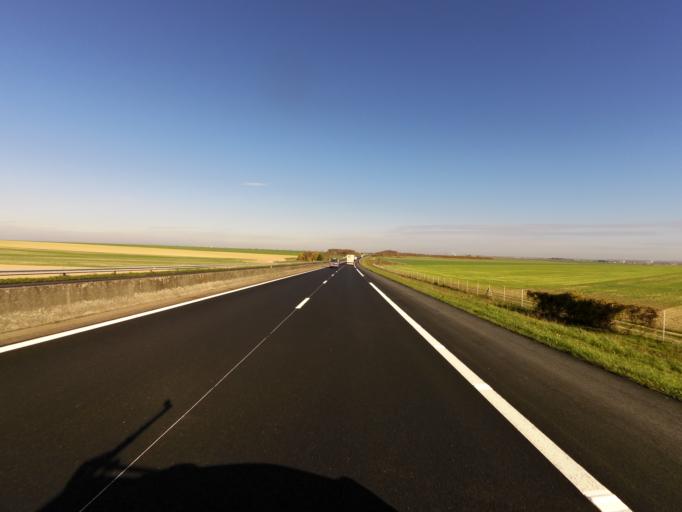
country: FR
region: Champagne-Ardenne
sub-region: Departement de la Marne
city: Fagnieres
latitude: 48.9290
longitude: 4.2841
